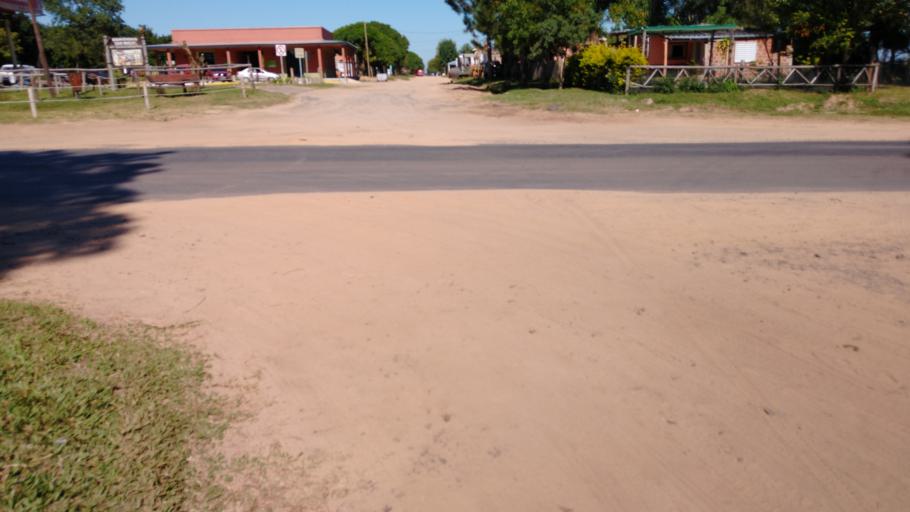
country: AR
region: Corrientes
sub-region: Departamento de San Miguel
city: San Miguel
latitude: -27.9919
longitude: -57.5958
